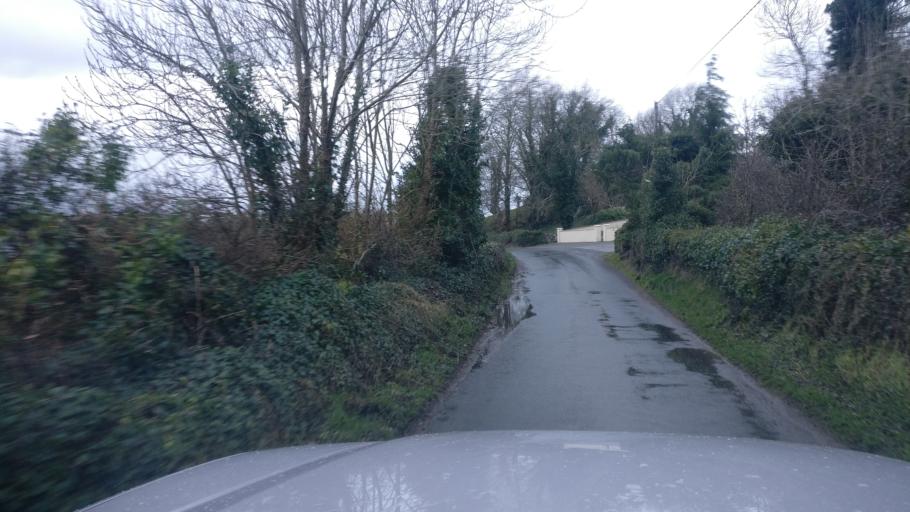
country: IE
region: Connaught
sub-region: County Galway
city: Athenry
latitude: 53.1854
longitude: -8.7073
